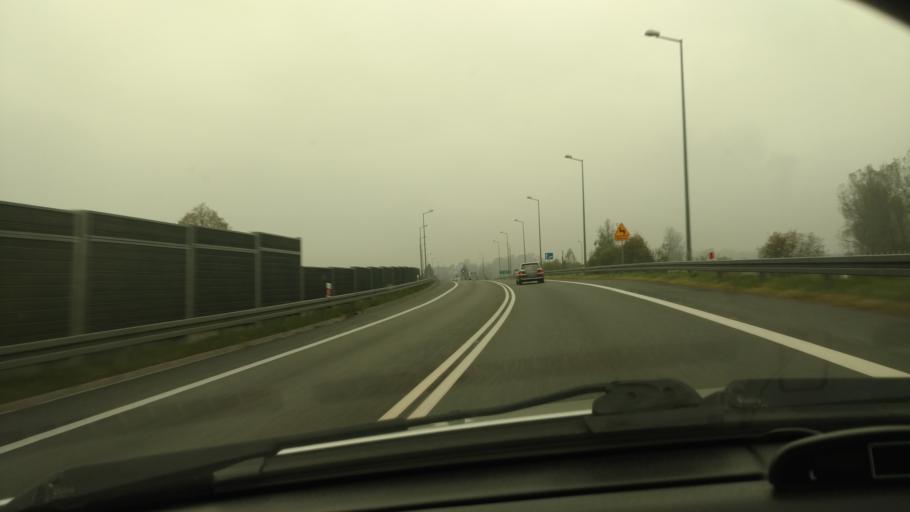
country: PL
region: Lesser Poland Voivodeship
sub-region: Powiat gorlicki
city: Biecz
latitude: 49.7095
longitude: 21.2408
